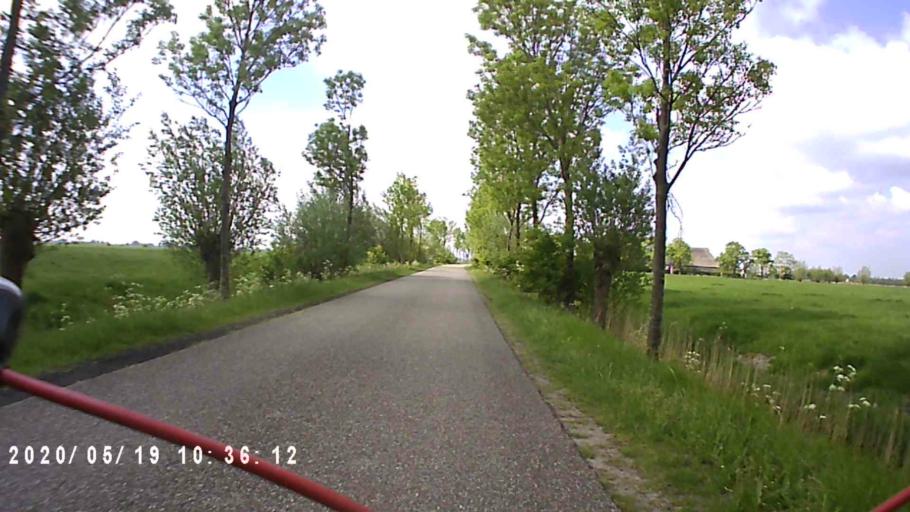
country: NL
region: Friesland
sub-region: Gemeente Kollumerland en Nieuwkruisland
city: Kollum
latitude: 53.2784
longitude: 6.1829
